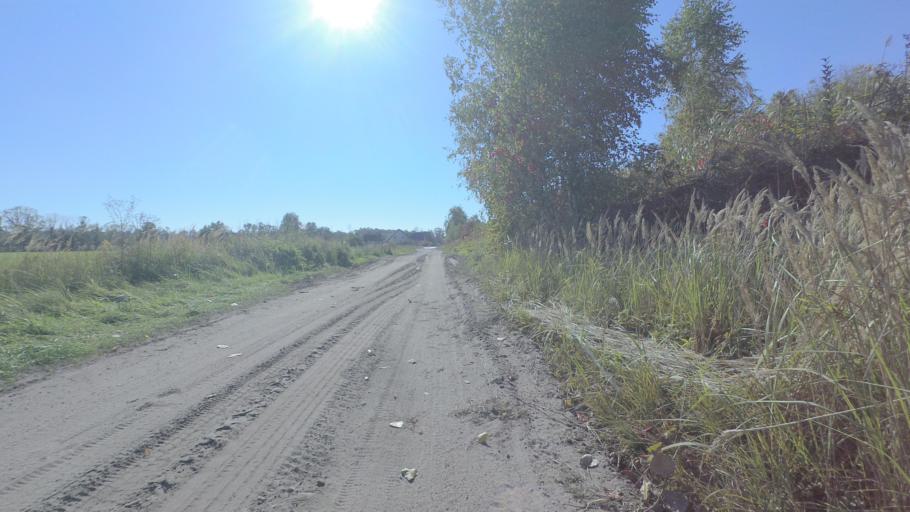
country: DE
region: Brandenburg
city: Sperenberg
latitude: 52.1507
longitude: 13.3707
